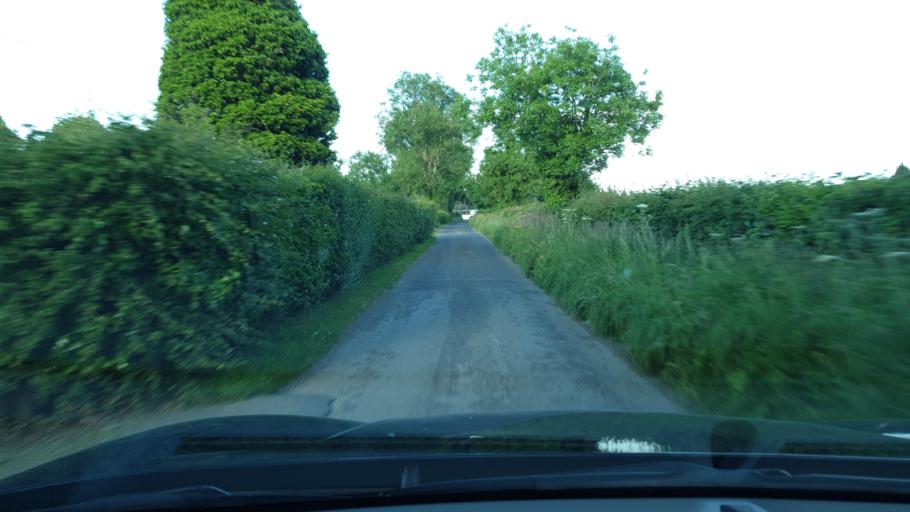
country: IE
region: Leinster
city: Hartstown
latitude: 53.4377
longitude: -6.3994
